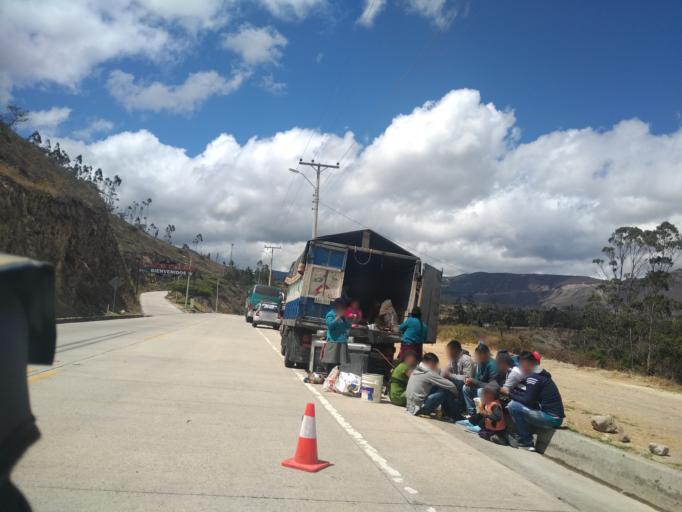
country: EC
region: El Oro
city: Zaruma
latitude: -3.4542
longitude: -79.1622
